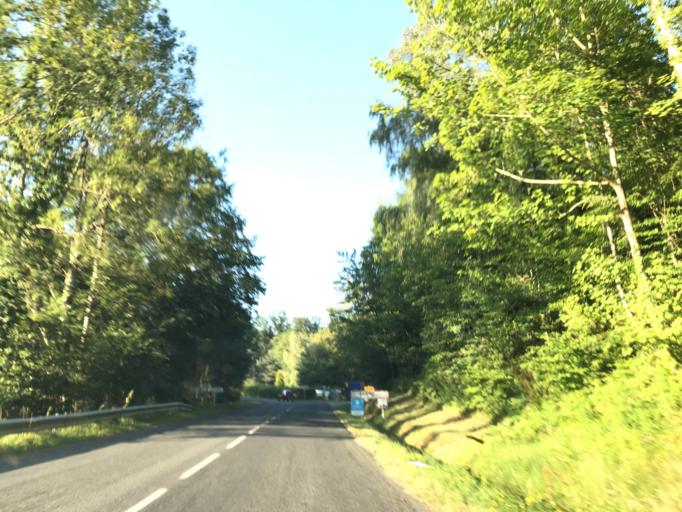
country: FR
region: Auvergne
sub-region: Departement du Puy-de-Dome
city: Saint-Remy-sur-Durolle
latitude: 45.8881
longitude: 3.6007
